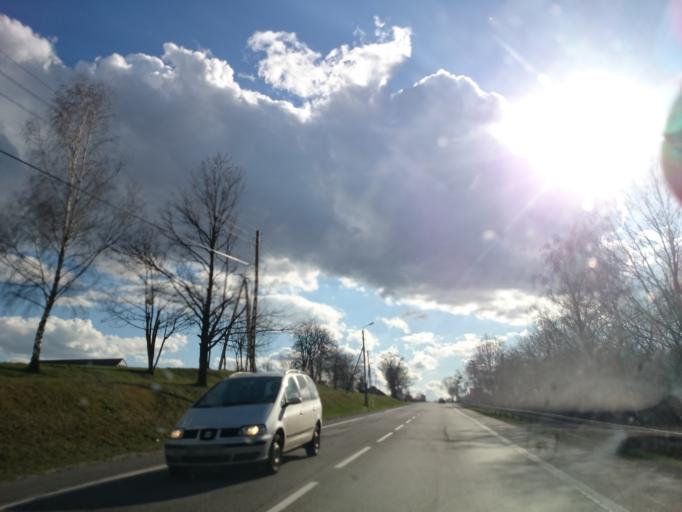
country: PL
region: Opole Voivodeship
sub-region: Powiat opolski
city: Niemodlin
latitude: 50.6406
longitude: 17.6085
